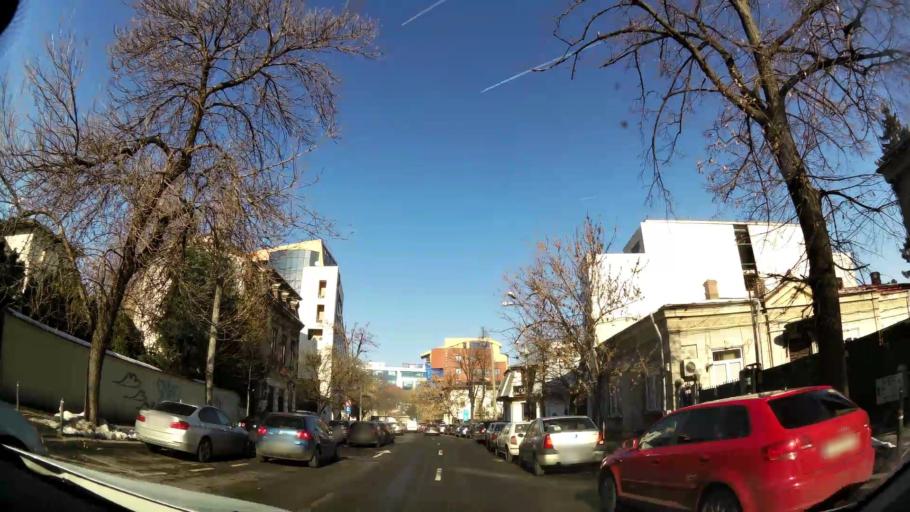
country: RO
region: Bucuresti
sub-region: Municipiul Bucuresti
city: Bucharest
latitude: 44.4490
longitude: 26.1029
